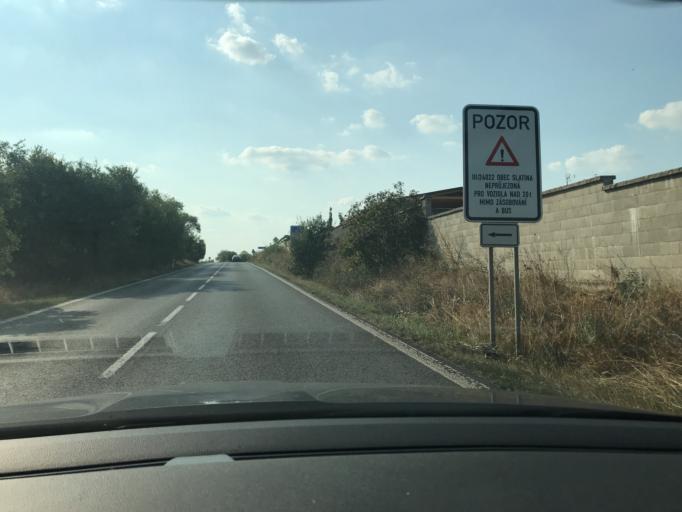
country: CZ
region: Central Bohemia
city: Nelahozeves
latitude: 50.2334
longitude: 14.2716
